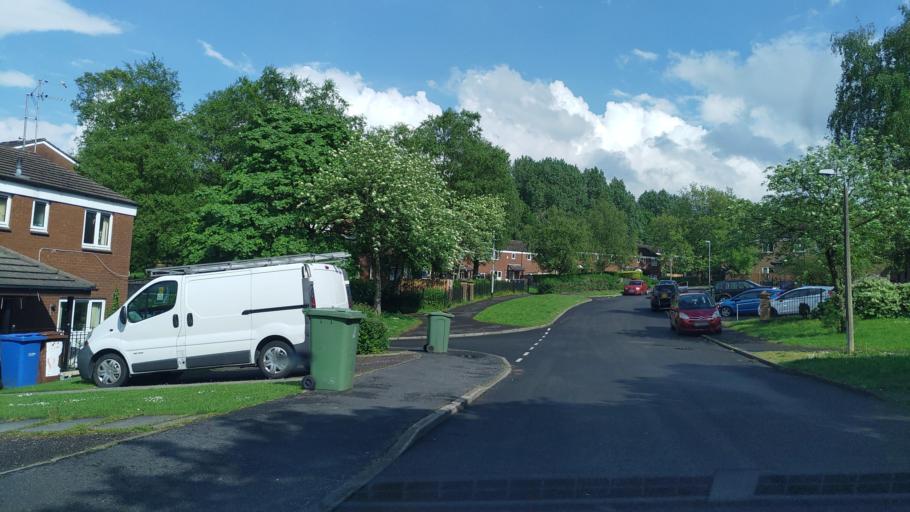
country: GB
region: England
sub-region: Lancashire
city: Clayton-le-Woods
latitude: 53.7158
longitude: -2.6371
